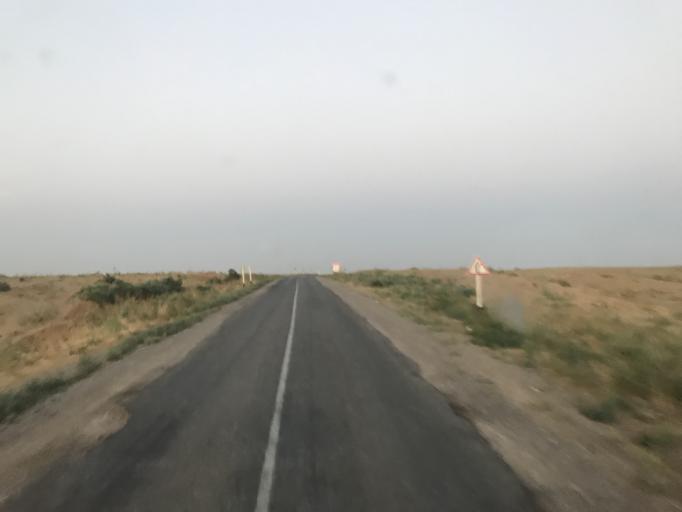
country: UZ
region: Toshkent
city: Chinoz
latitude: 41.1987
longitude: 68.6110
